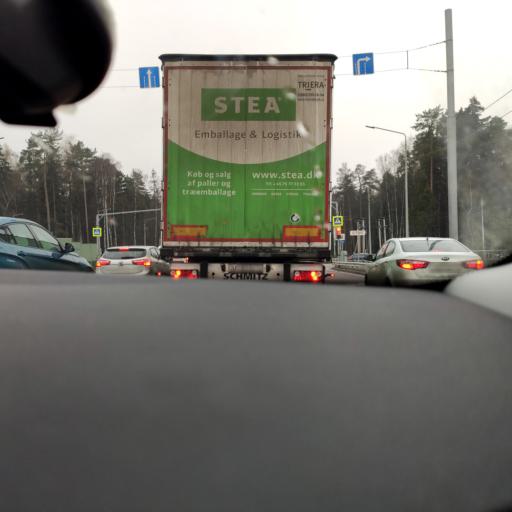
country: RU
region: Moskovskaya
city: Pavlovskaya Sloboda
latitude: 55.8079
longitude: 37.1292
